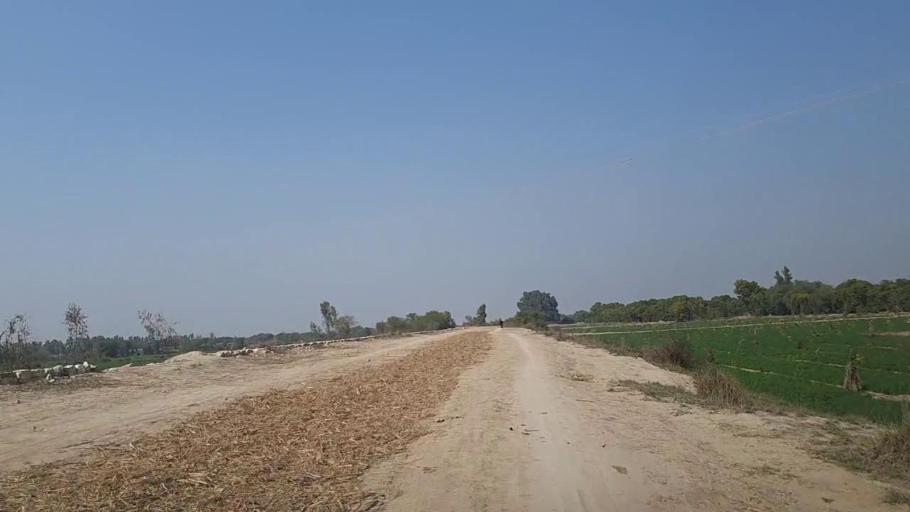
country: PK
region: Sindh
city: Moro
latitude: 26.8180
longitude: 67.9539
